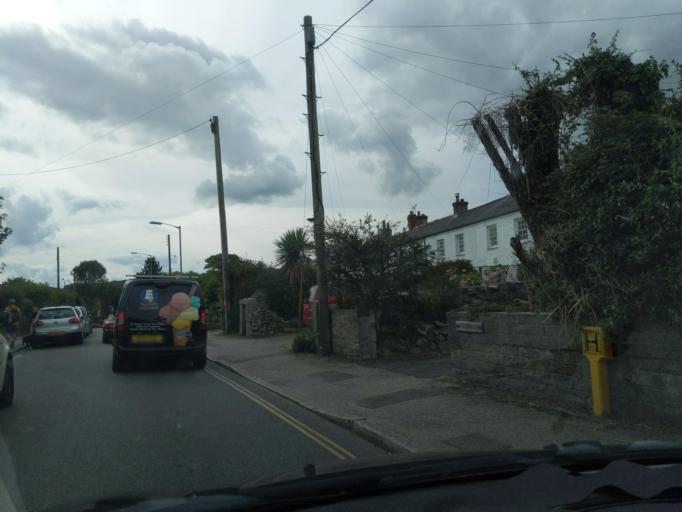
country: GB
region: England
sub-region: Cornwall
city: St Austell
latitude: 50.3362
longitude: -4.7604
